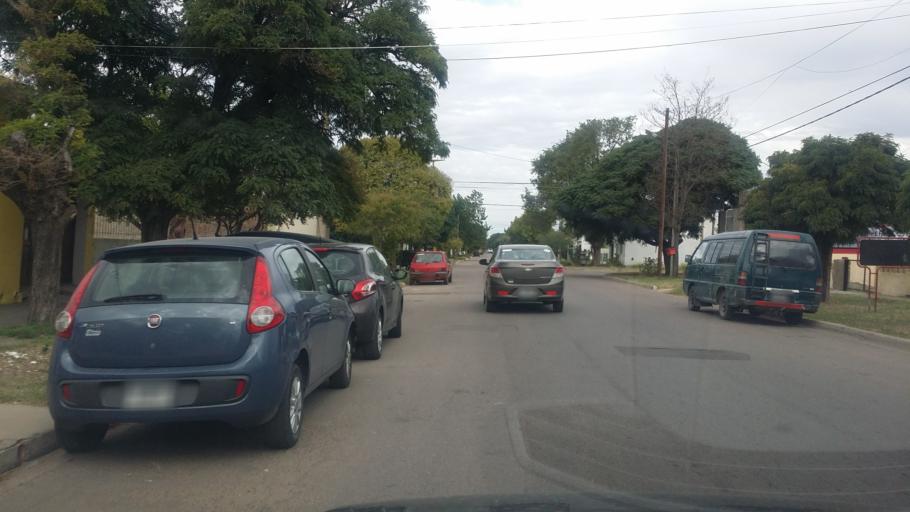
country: AR
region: La Pampa
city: Santa Rosa
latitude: -36.6334
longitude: -64.2868
